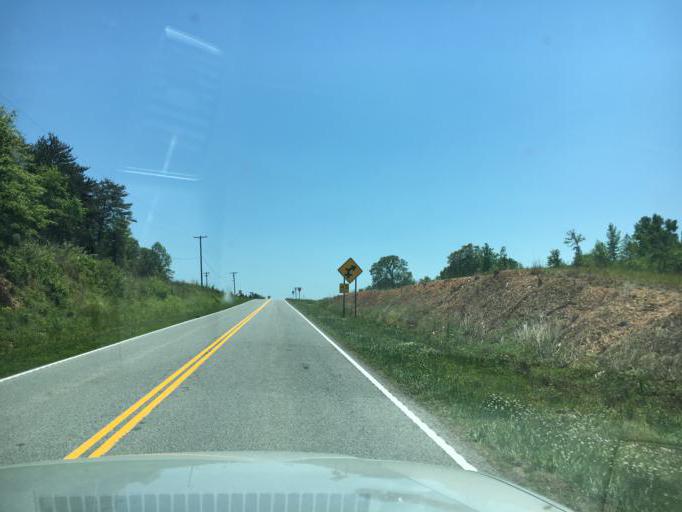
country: US
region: South Carolina
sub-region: Cherokee County
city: Blacksburg
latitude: 35.1530
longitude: -81.5744
